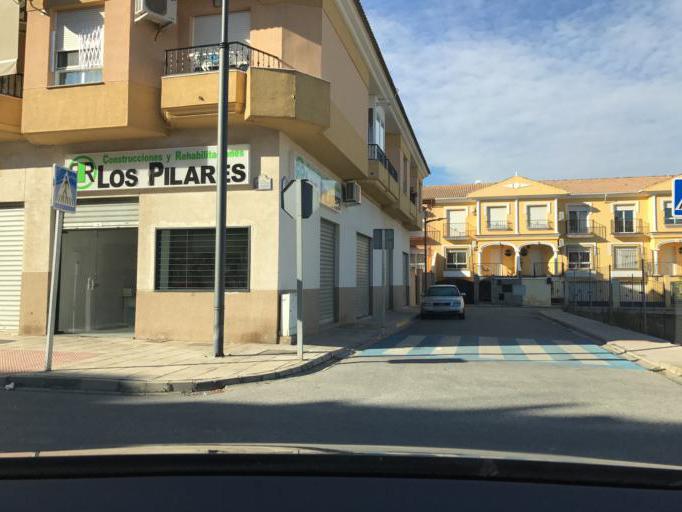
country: ES
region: Andalusia
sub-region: Provincia de Granada
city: Churriana de la Vega
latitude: 37.1480
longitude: -3.6517
